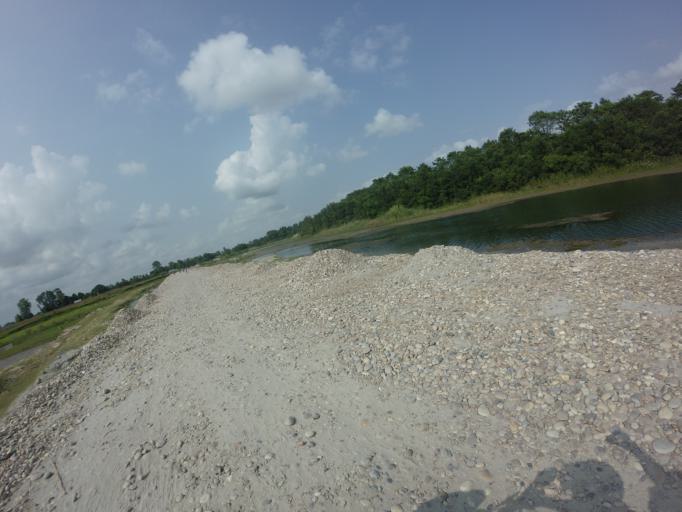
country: NP
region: Far Western
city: Tikapur
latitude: 28.4486
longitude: 81.0740
